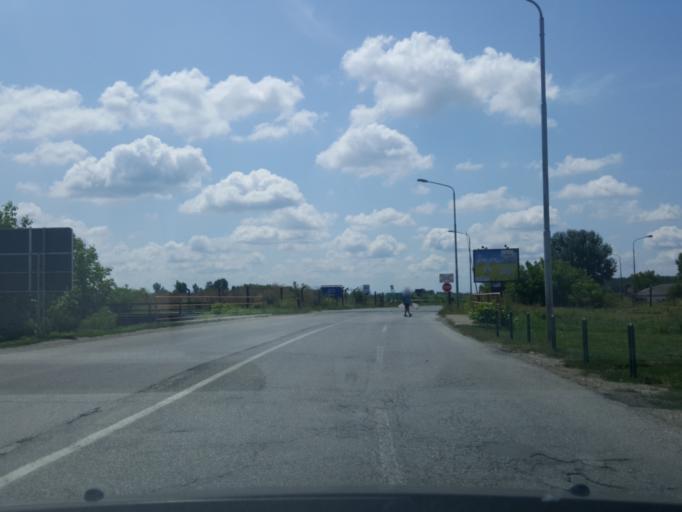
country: RS
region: Autonomna Pokrajina Vojvodina
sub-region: Sremski Okrug
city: Sremska Mitrovica
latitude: 44.9700
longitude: 19.6368
